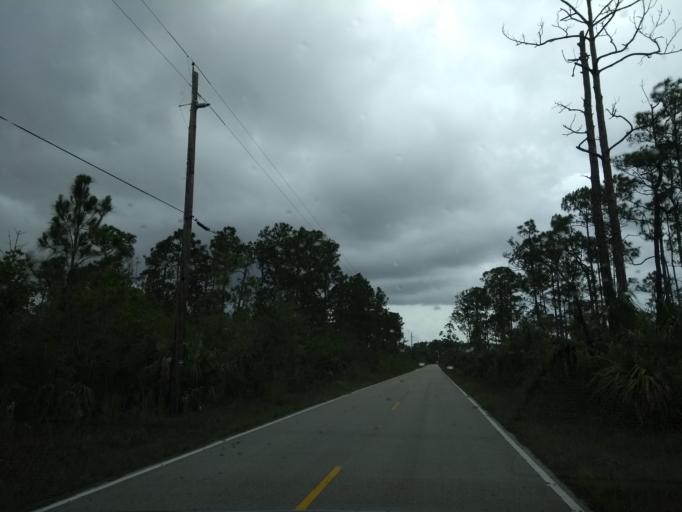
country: US
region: Florida
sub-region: Miami-Dade County
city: The Hammocks
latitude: 25.7490
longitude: -80.9371
